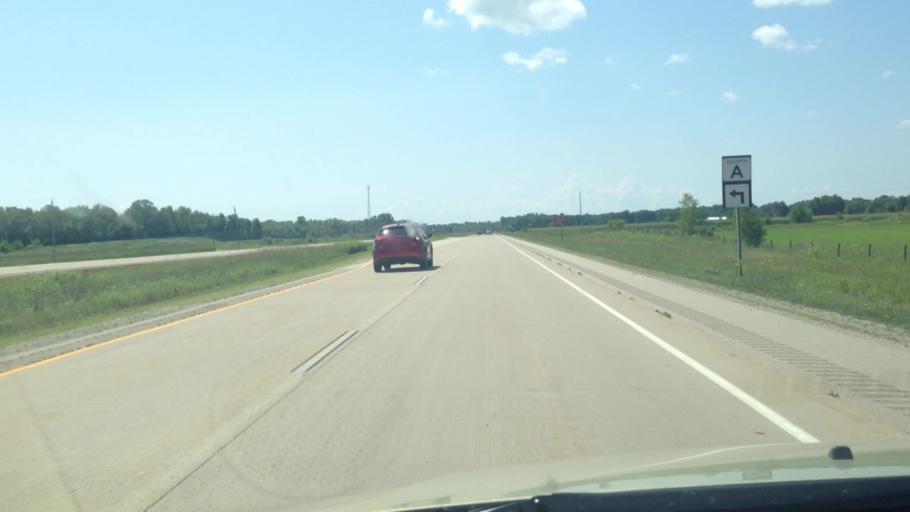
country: US
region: Wisconsin
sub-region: Oconto County
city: Oconto
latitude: 44.9441
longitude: -87.8710
